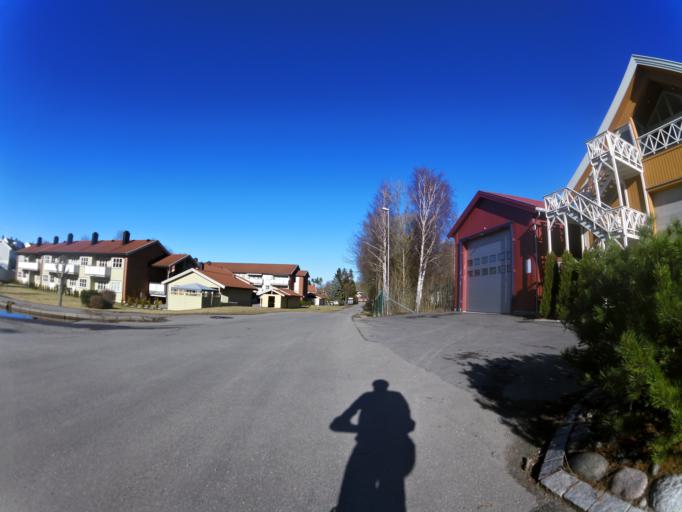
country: NO
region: Ostfold
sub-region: Fredrikstad
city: Fredrikstad
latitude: 59.2132
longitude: 10.9075
